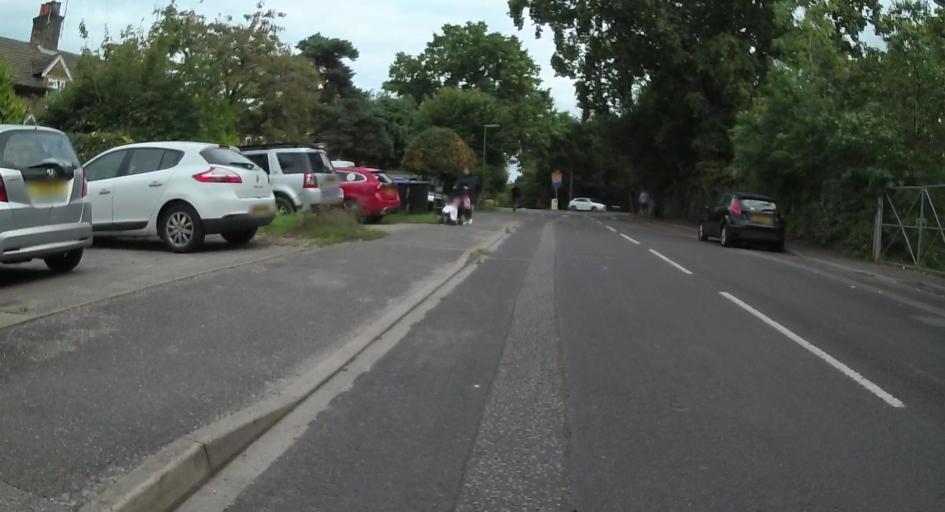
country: GB
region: England
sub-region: Surrey
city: Knaphill
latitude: 51.3156
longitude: -0.6060
